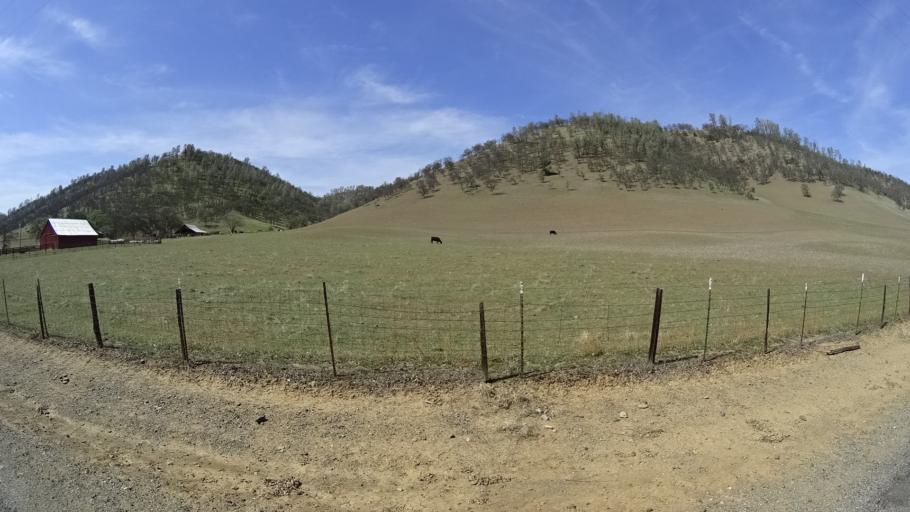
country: US
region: California
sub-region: Glenn County
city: Willows
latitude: 39.5080
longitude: -122.4537
